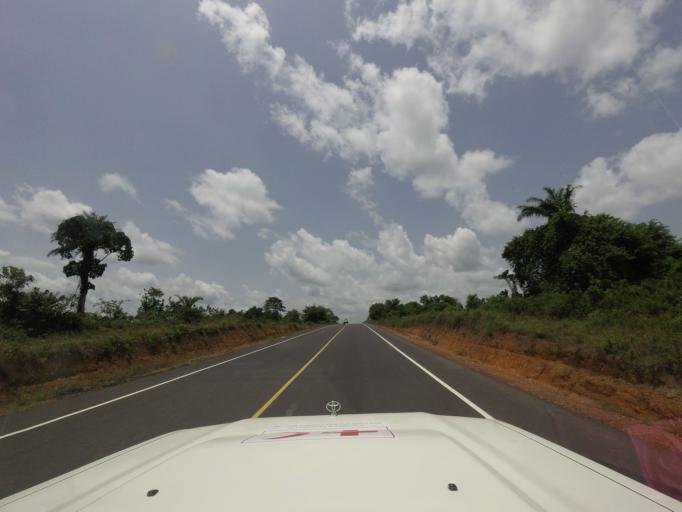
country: LR
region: Margibi
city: Kakata
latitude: 6.4726
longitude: -10.4072
